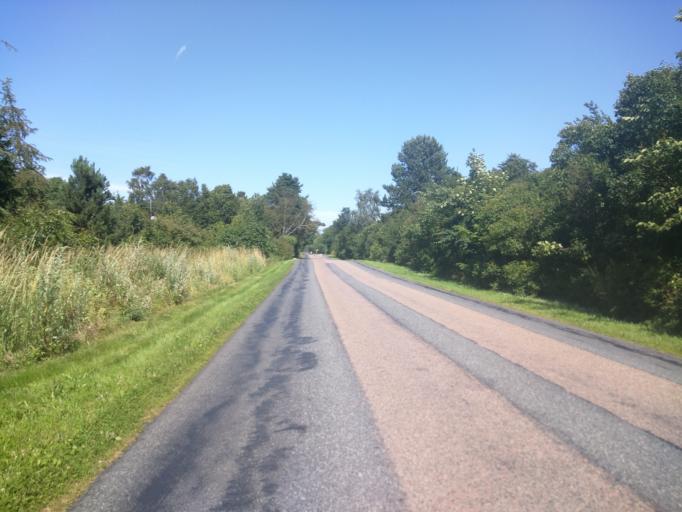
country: DK
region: Zealand
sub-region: Kalundborg Kommune
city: Svebolle
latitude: 55.6958
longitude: 11.2527
